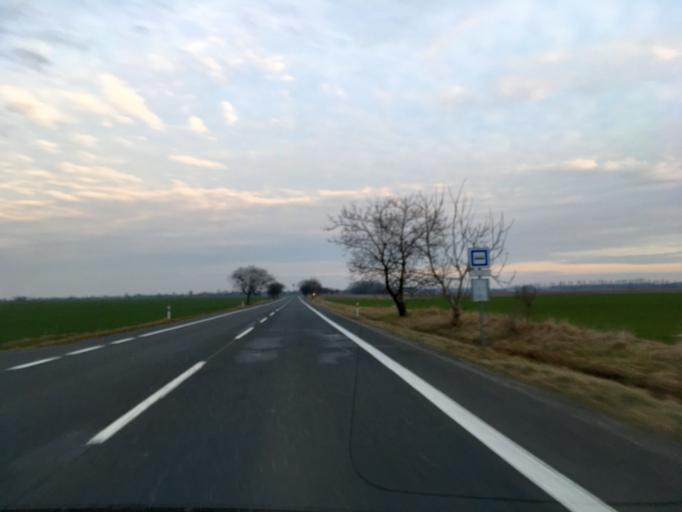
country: HU
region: Komarom-Esztergom
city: Acs
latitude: 47.7765
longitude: 17.9436
